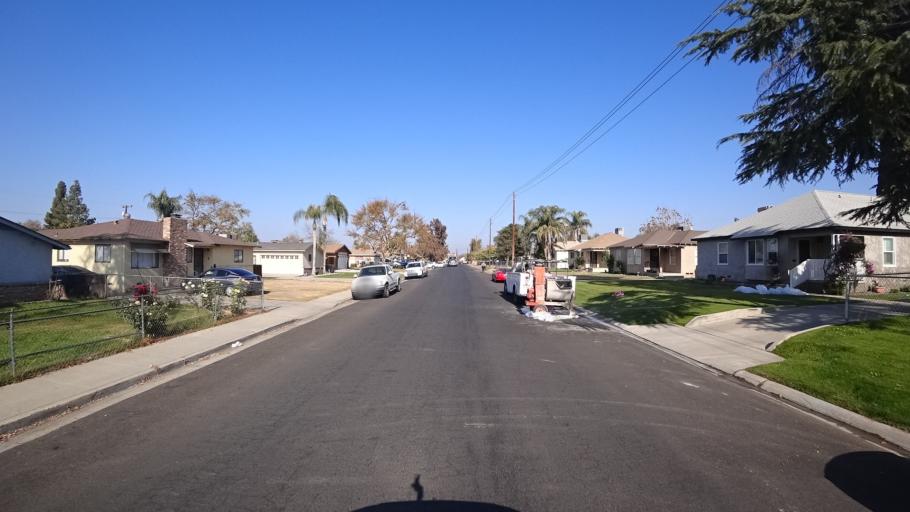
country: US
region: California
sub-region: Kern County
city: Bakersfield
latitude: 35.3478
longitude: -119.0345
